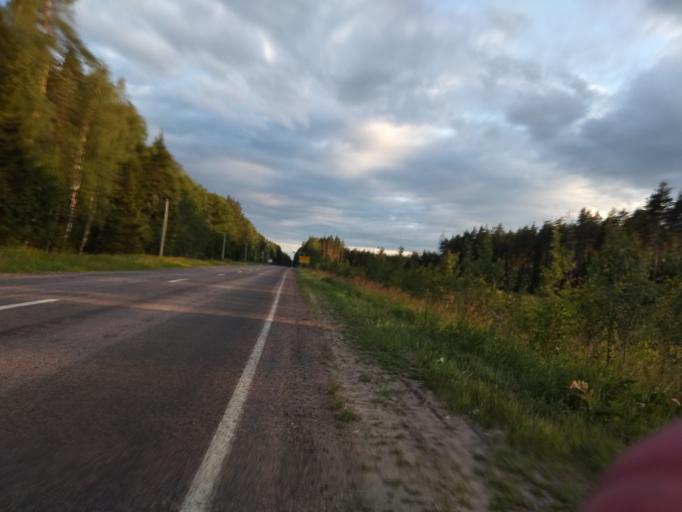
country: RU
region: Moskovskaya
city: Misheronskiy
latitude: 55.6202
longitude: 39.7283
